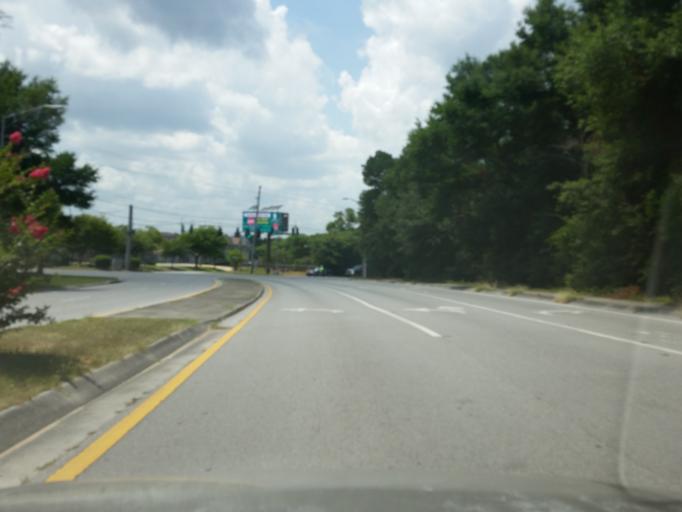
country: US
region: Florida
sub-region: Escambia County
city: Goulding
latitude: 30.4681
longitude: -87.2014
